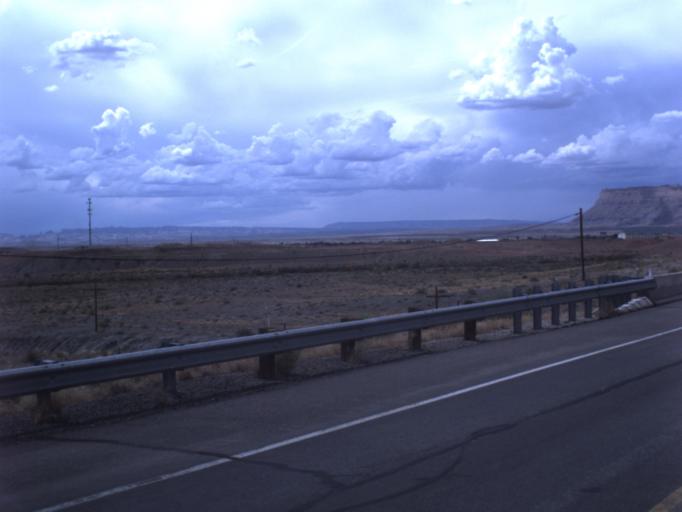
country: US
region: Utah
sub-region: Carbon County
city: East Carbon City
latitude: 38.9835
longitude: -110.1243
